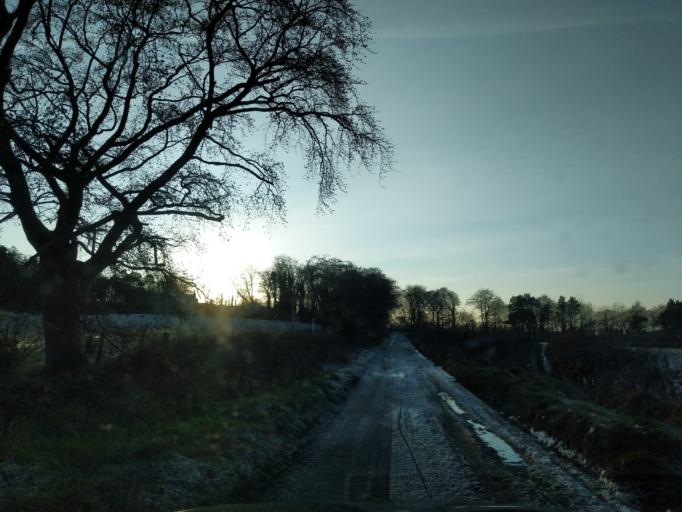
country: GB
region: Scotland
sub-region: Edinburgh
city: Balerno
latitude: 55.8644
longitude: -3.3658
